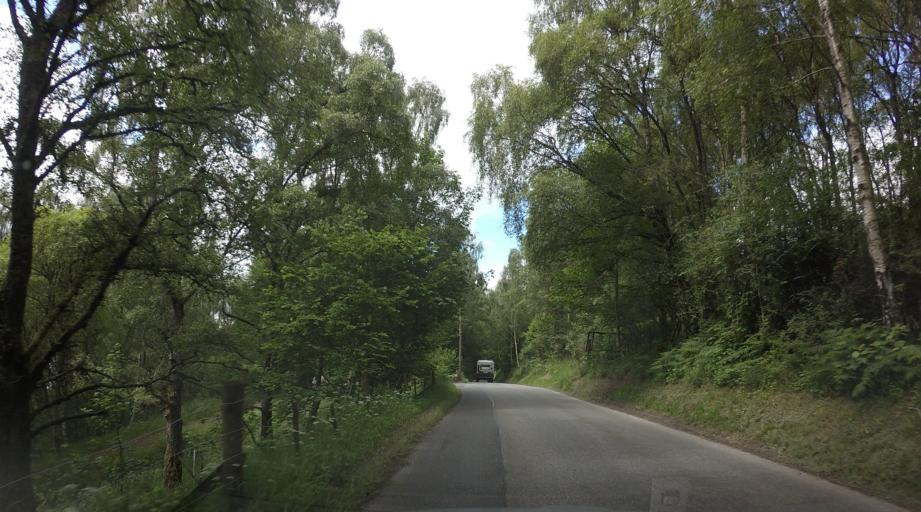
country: GB
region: Scotland
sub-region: Perth and Kinross
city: Aberfeldy
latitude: 56.7179
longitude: -3.9245
